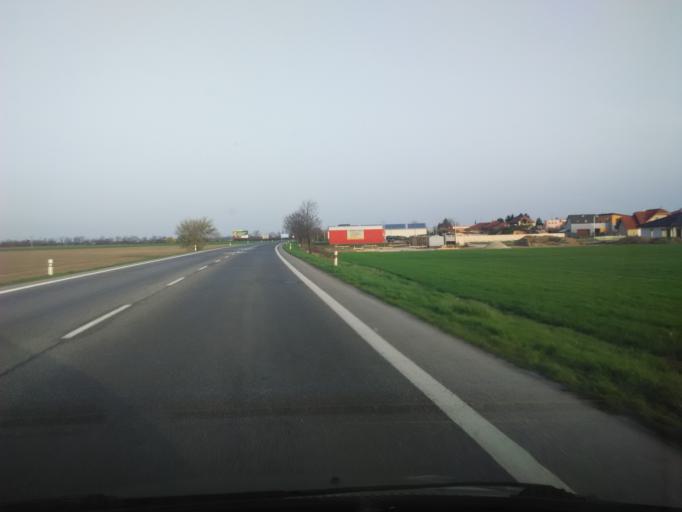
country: SK
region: Nitriansky
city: Sellye
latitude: 48.1586
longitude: 17.8526
